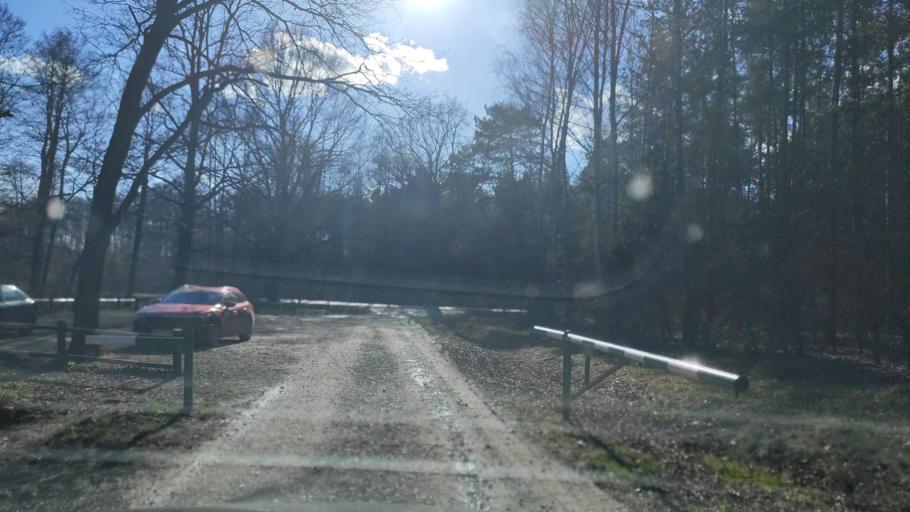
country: PL
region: Masovian Voivodeship
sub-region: Powiat radomski
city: Jastrzebia
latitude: 51.4655
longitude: 21.2309
